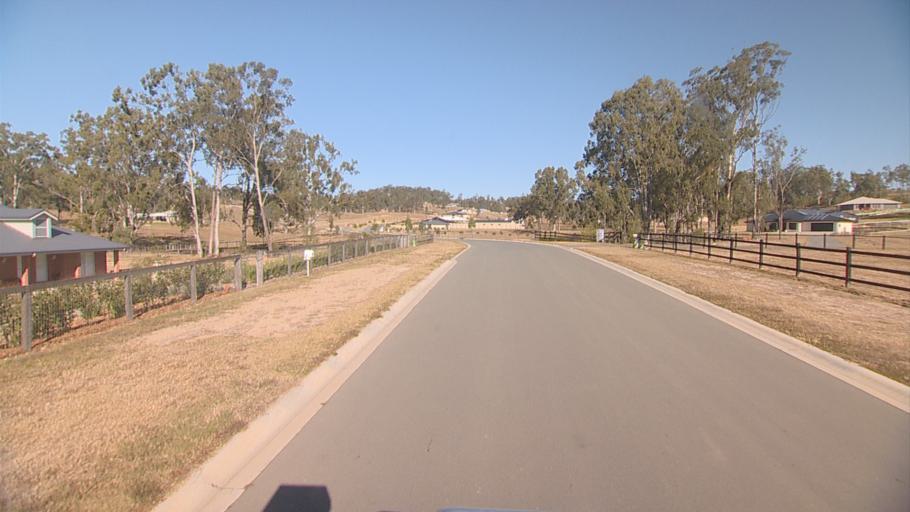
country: AU
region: Queensland
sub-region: Logan
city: Cedar Vale
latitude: -27.8688
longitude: 153.0553
